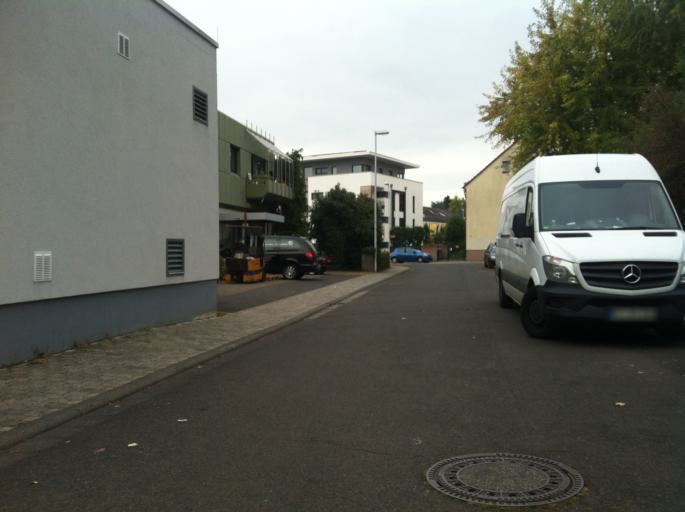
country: DE
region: Rheinland-Pfalz
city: Mainz
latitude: 49.9819
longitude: 8.2931
